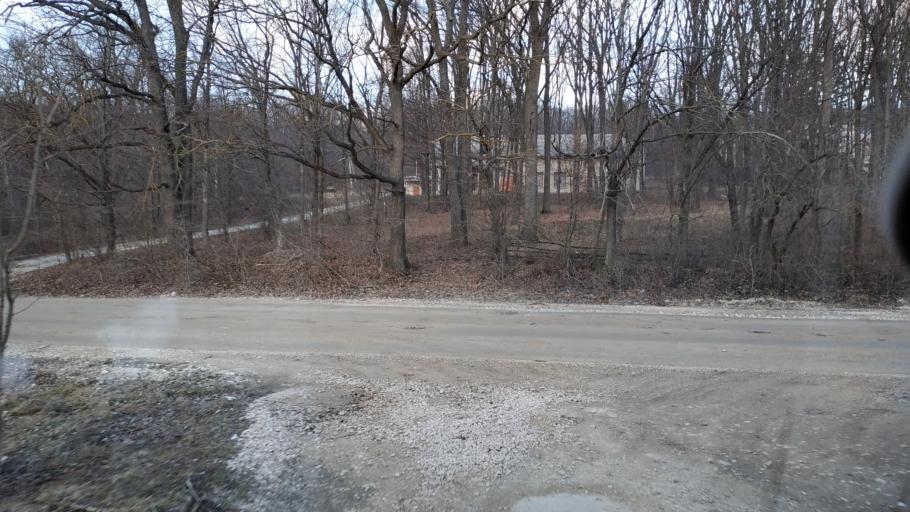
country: MD
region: Calarasi
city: Calarasi
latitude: 47.3305
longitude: 28.2228
